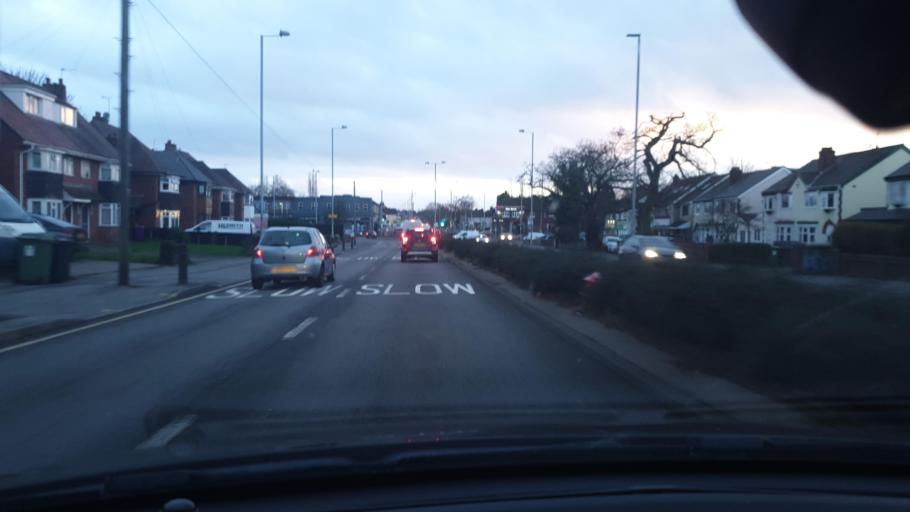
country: GB
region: England
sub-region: Wolverhampton
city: Wolverhampton
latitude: 52.6223
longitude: -2.1288
